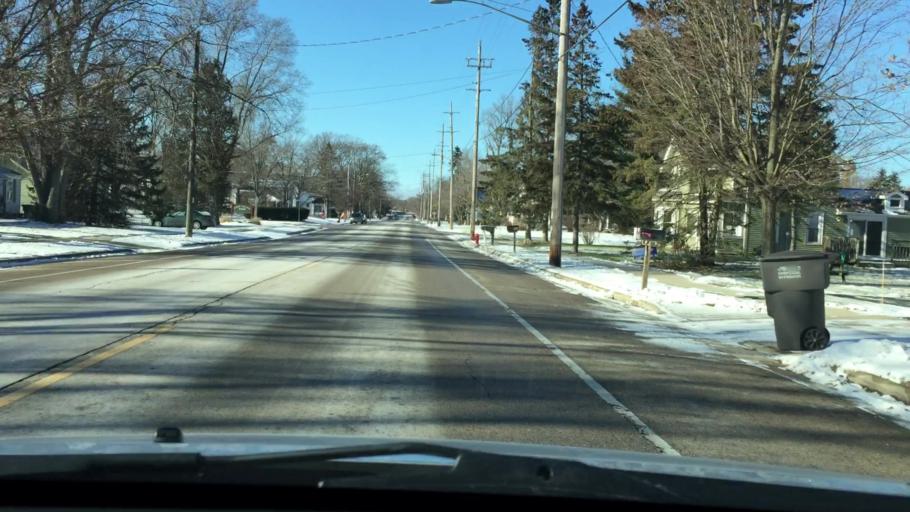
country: US
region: Wisconsin
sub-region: Waukesha County
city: Eagle
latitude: 42.8790
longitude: -88.4672
